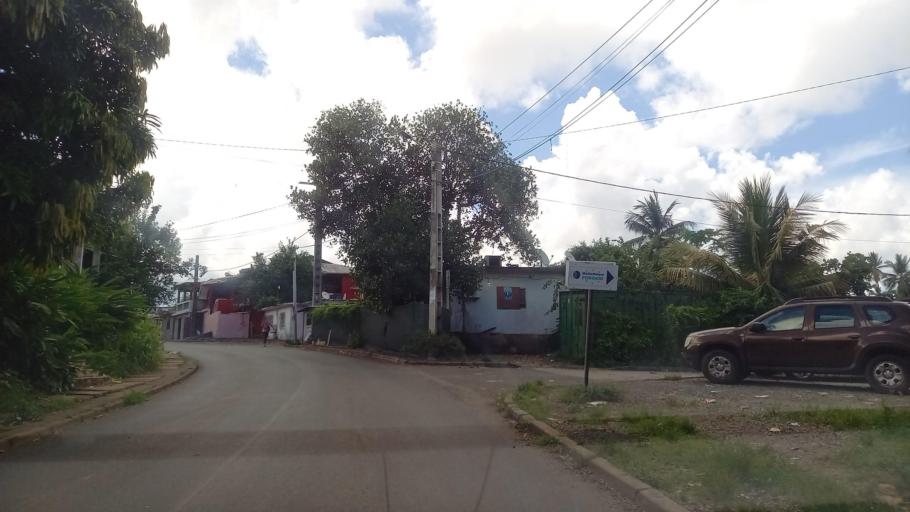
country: YT
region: Chirongui
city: Chirongui
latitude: -12.8907
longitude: 45.1392
